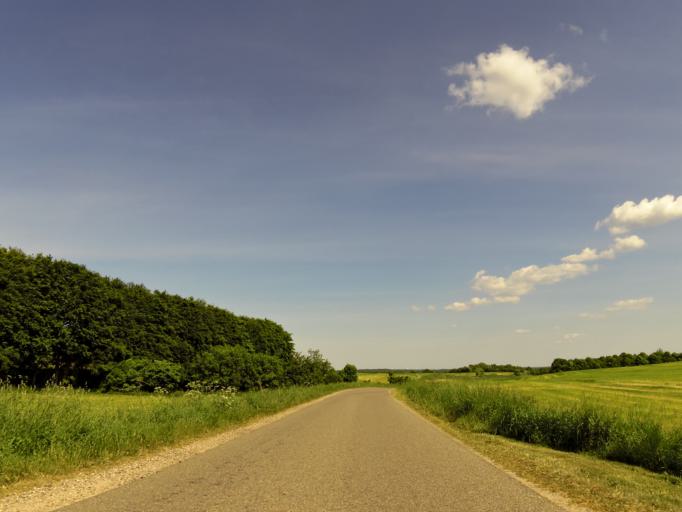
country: DK
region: Central Jutland
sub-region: Holstebro Kommune
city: Vinderup
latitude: 56.4366
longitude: 8.8764
